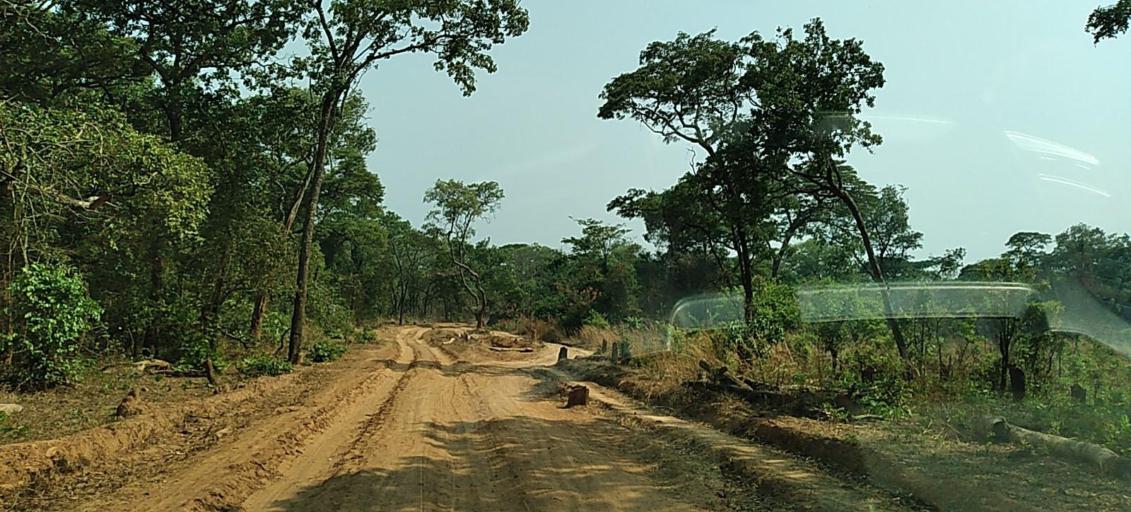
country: ZM
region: North-Western
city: Kansanshi
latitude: -12.0762
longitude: 26.8878
